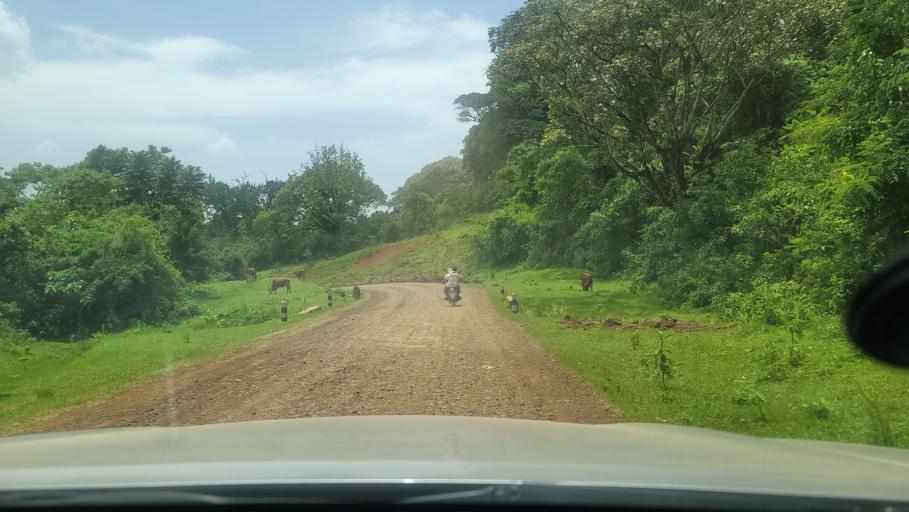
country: ET
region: Oromiya
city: Agaro
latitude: 7.7192
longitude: 36.2601
